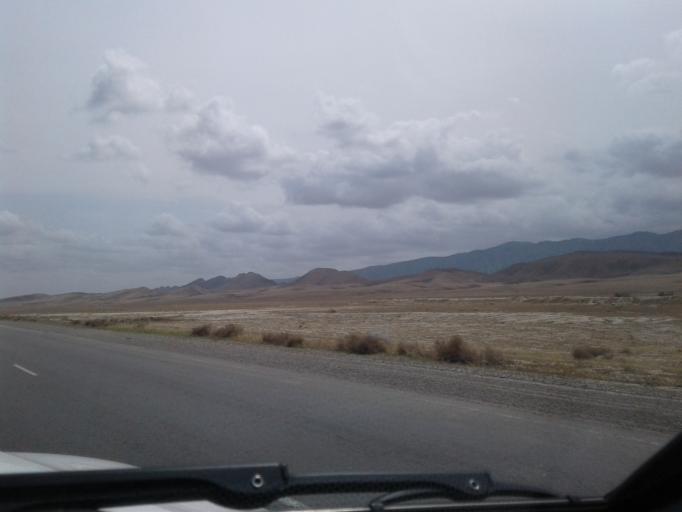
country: IR
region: Razavi Khorasan
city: Dargaz
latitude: 37.7016
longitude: 59.0414
